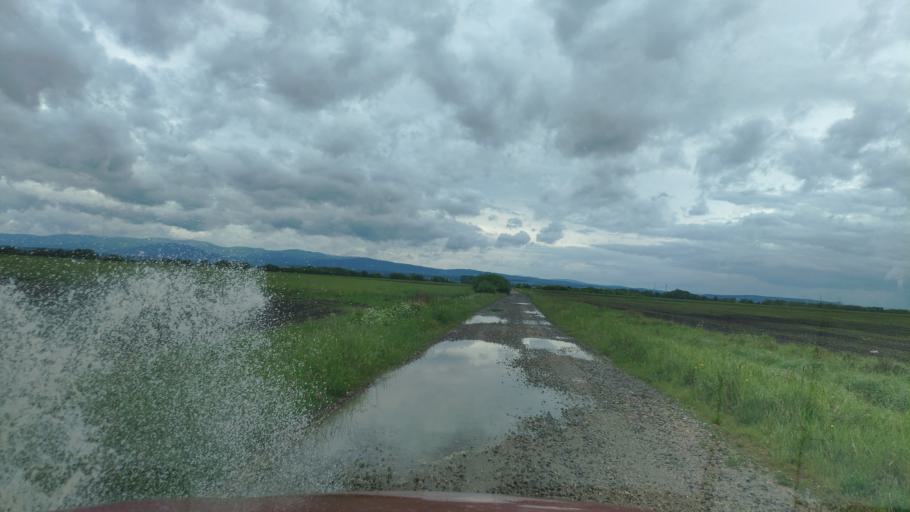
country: SK
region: Kosicky
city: Moldava nad Bodvou
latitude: 48.5479
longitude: 21.1133
